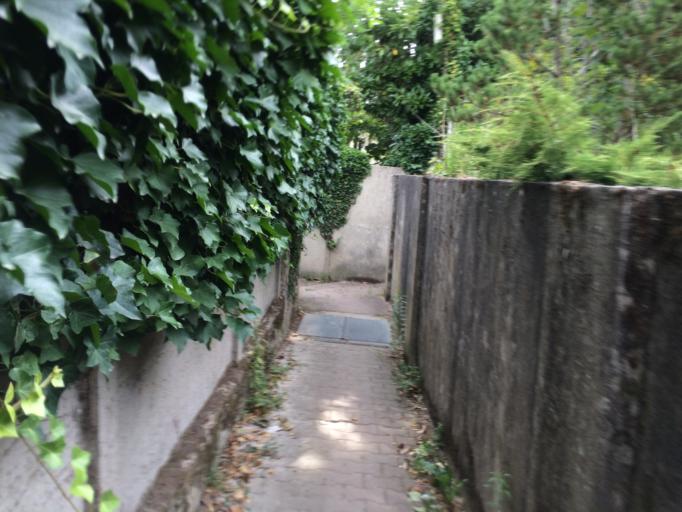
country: FR
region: Ile-de-France
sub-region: Departement de l'Essonne
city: Orsay
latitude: 48.7070
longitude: 2.2118
